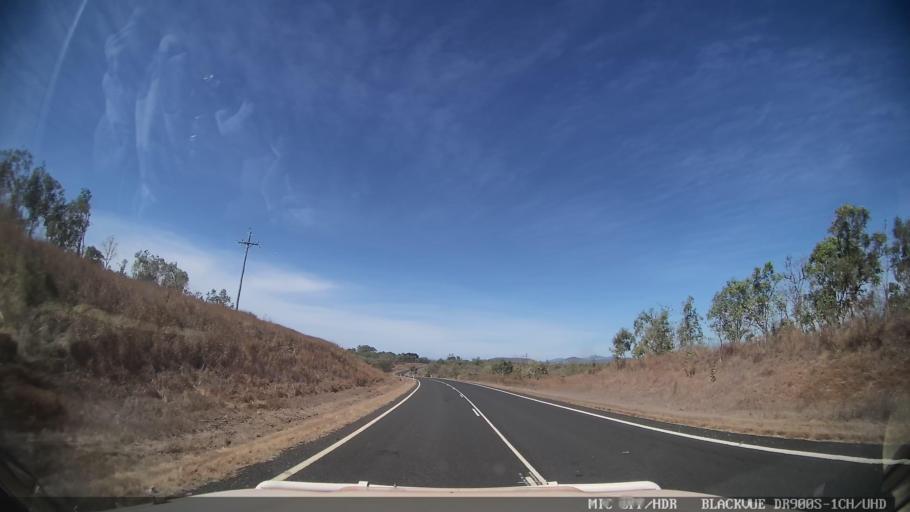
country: AU
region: Queensland
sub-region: Cook
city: Cooktown
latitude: -15.8657
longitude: 144.8164
